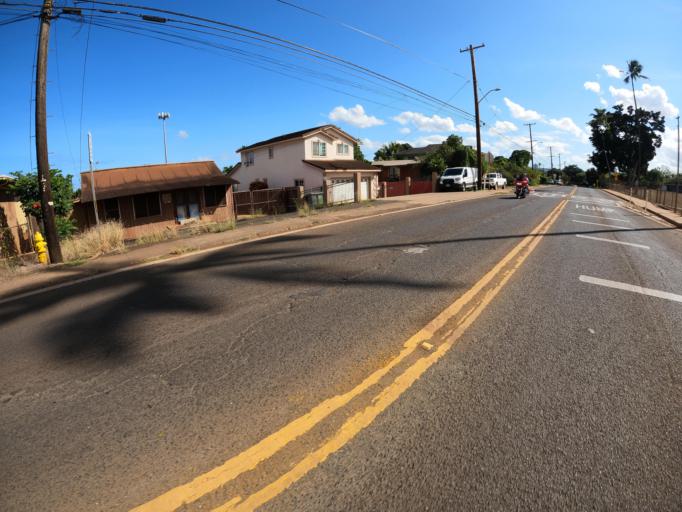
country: US
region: Hawaii
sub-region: Honolulu County
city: Waialua
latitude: 21.5671
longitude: -158.1259
